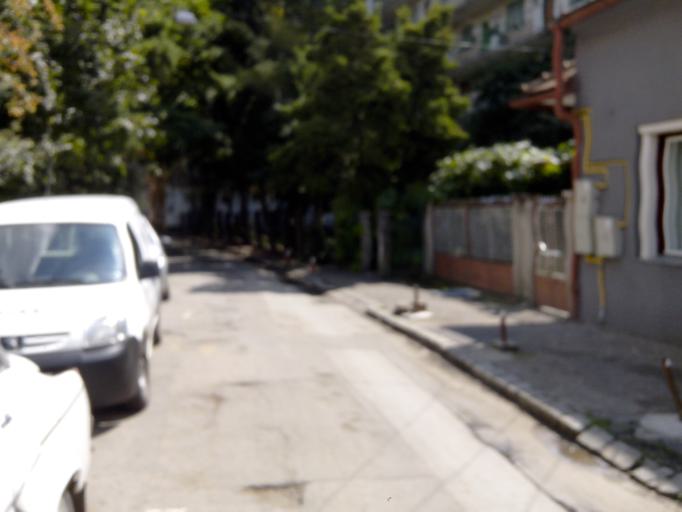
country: RO
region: Cluj
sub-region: Municipiul Cluj-Napoca
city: Cluj-Napoca
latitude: 46.7818
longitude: 23.5866
